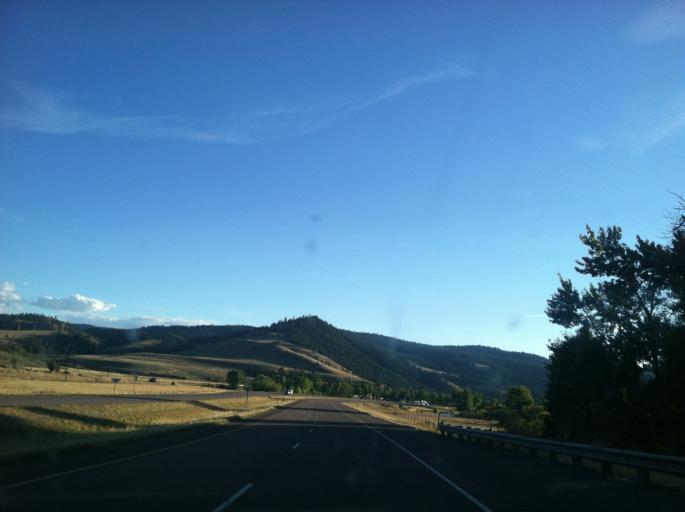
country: US
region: Montana
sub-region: Granite County
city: Philipsburg
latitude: 46.7080
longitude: -113.3347
